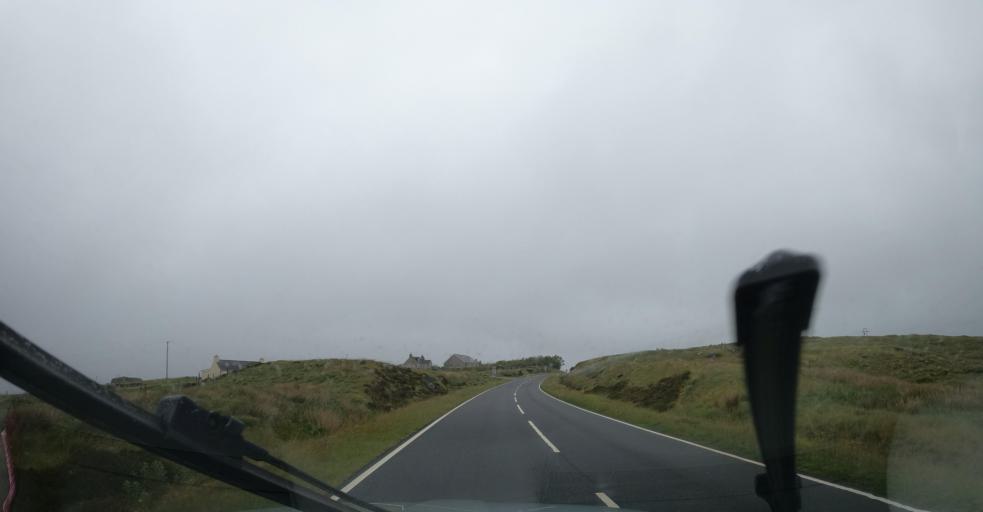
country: GB
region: Scotland
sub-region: Eilean Siar
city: Isle of North Uist
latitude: 57.6034
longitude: -7.1782
